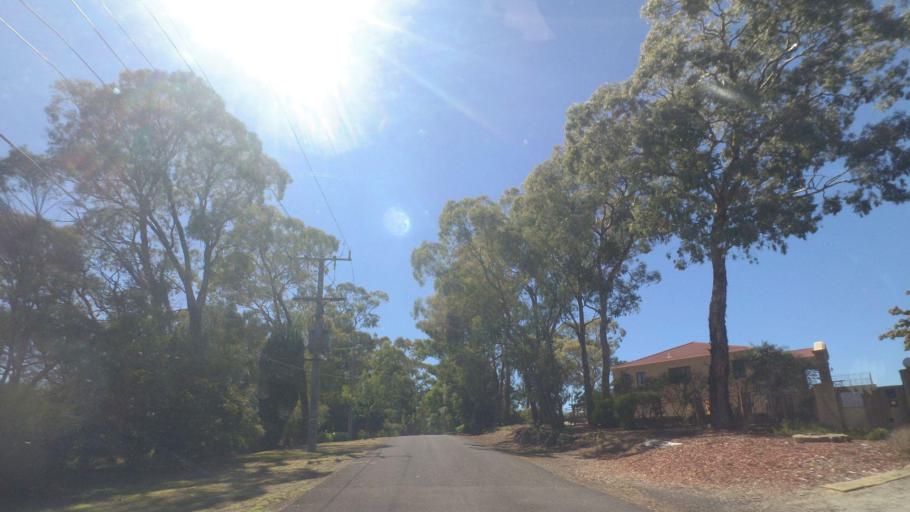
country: AU
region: Victoria
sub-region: Manningham
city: Donvale
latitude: -37.7889
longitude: 145.1916
